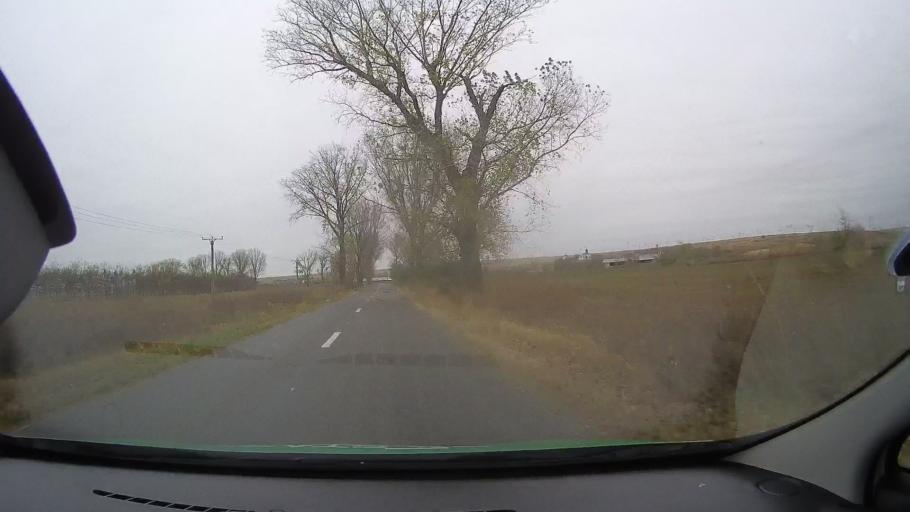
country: RO
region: Constanta
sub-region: Comuna Saraiu
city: Saraiu
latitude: 44.7238
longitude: 28.2207
